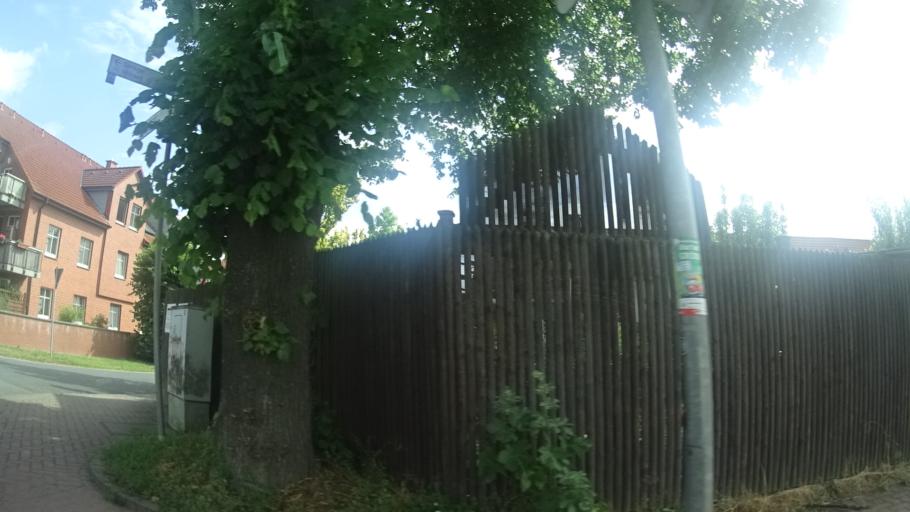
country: DE
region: Lower Saxony
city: Ronnenberg
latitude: 52.2365
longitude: 9.6729
